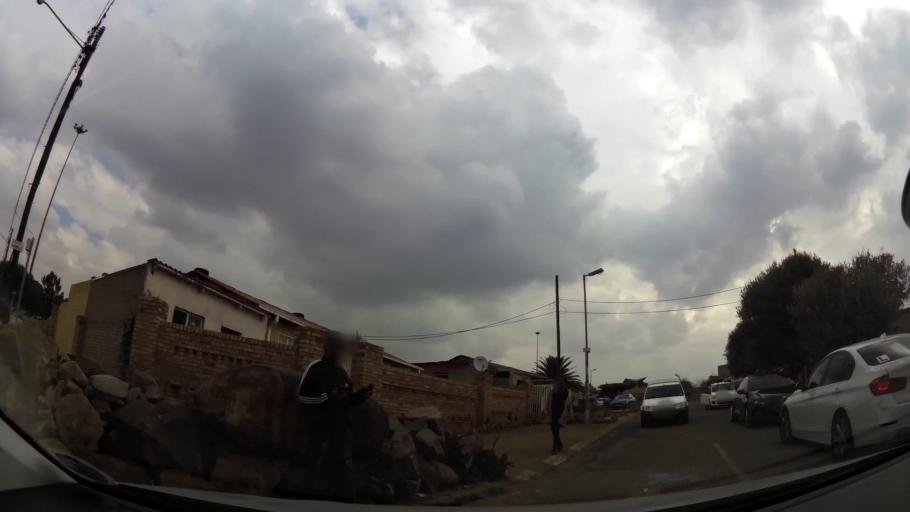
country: ZA
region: Gauteng
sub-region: City of Johannesburg Metropolitan Municipality
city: Soweto
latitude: -26.2646
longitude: 27.8632
